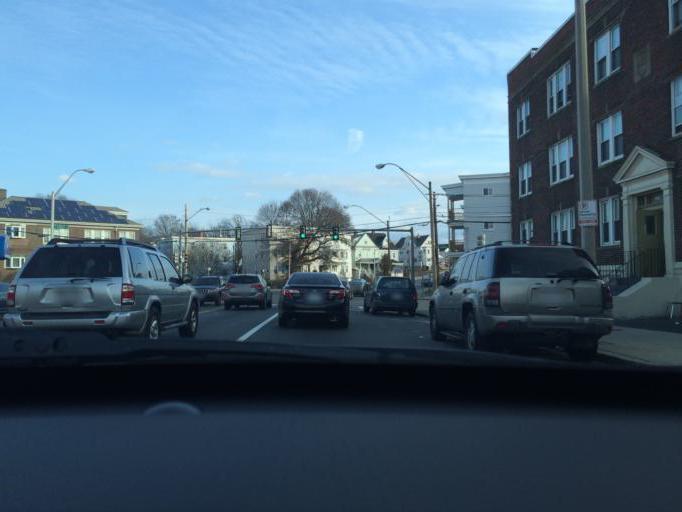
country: US
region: Massachusetts
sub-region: Norfolk County
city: Milton
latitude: 42.2806
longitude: -71.0834
